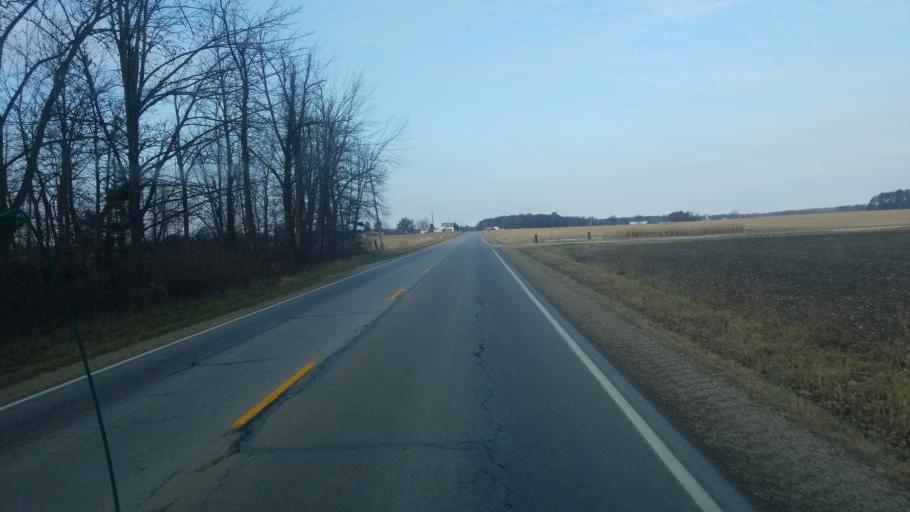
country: US
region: Indiana
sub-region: Adams County
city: Geneva
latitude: 40.5410
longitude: -84.9714
